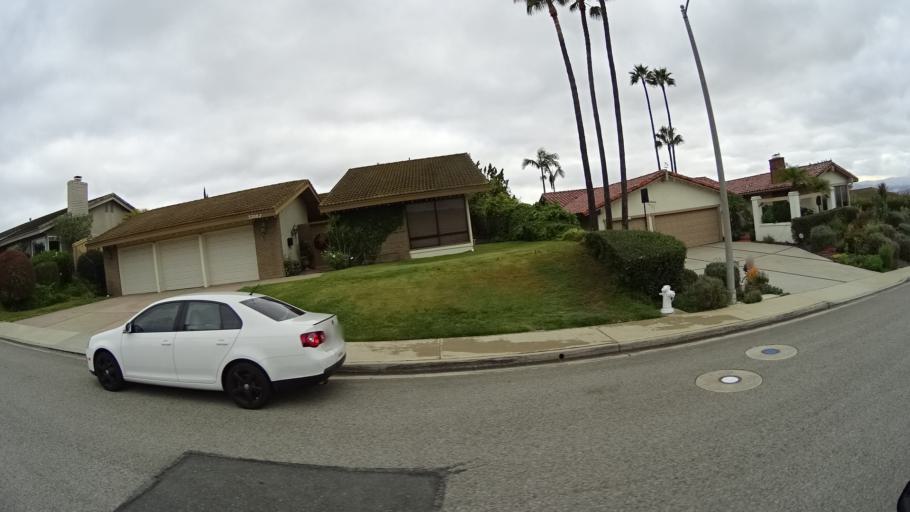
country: US
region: California
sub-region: Orange County
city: Laguna Niguel
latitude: 33.4962
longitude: -117.7270
